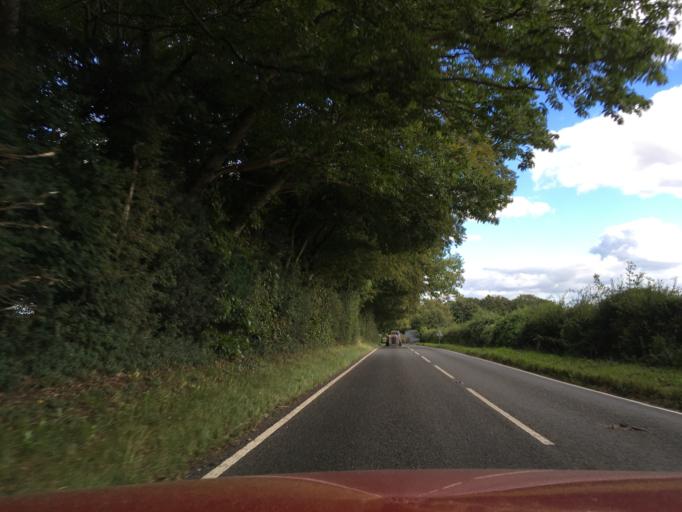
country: GB
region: England
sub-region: Hampshire
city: Chandlers Ford
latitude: 51.1037
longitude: -1.4130
